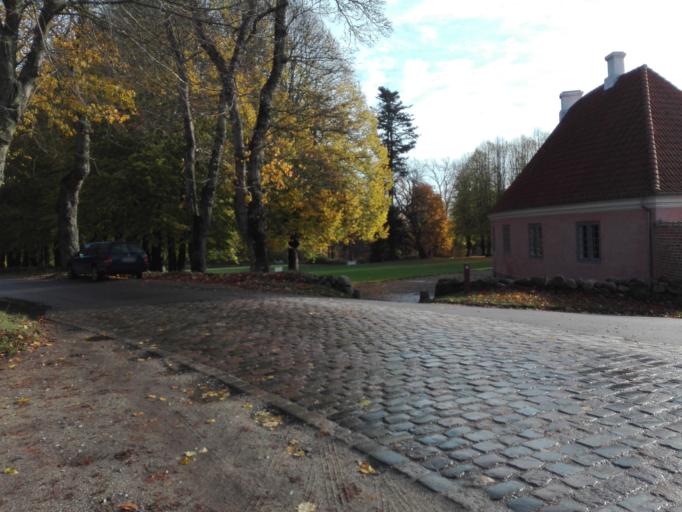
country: DK
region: Central Jutland
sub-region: Arhus Kommune
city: Beder
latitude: 56.0880
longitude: 10.2259
